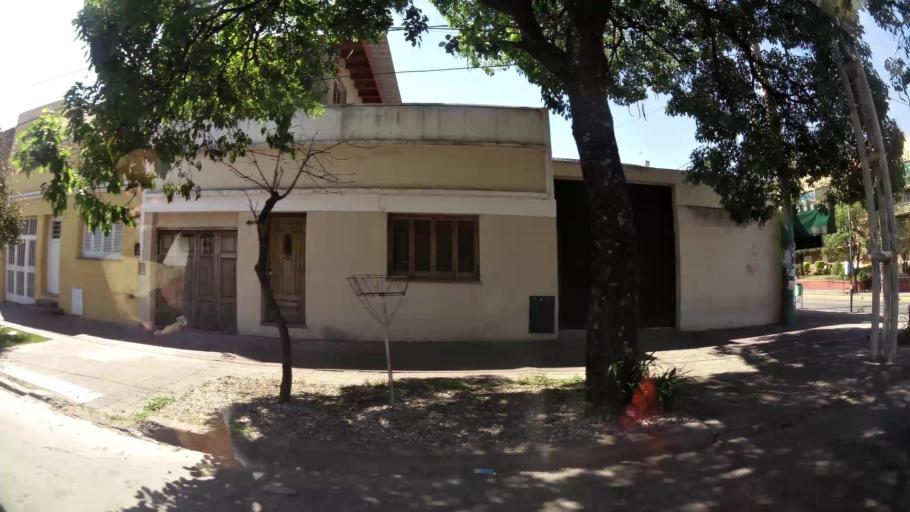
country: AR
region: Cordoba
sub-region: Departamento de Capital
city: Cordoba
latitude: -31.4082
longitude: -64.1585
